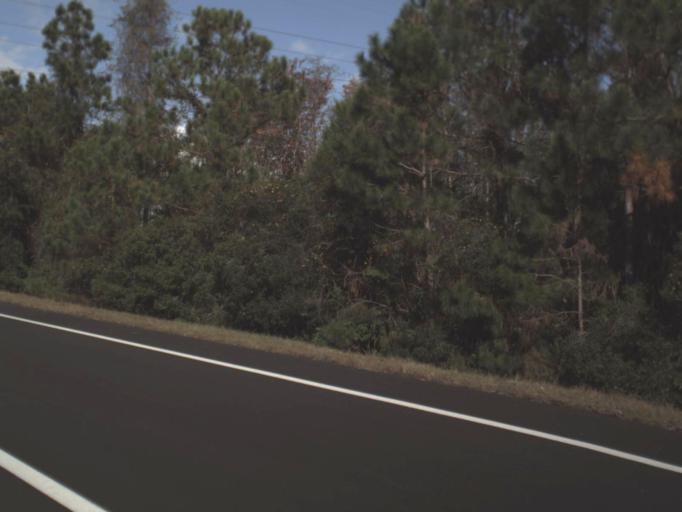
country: US
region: Florida
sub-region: Volusia County
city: Port Orange
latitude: 29.1278
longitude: -81.0465
